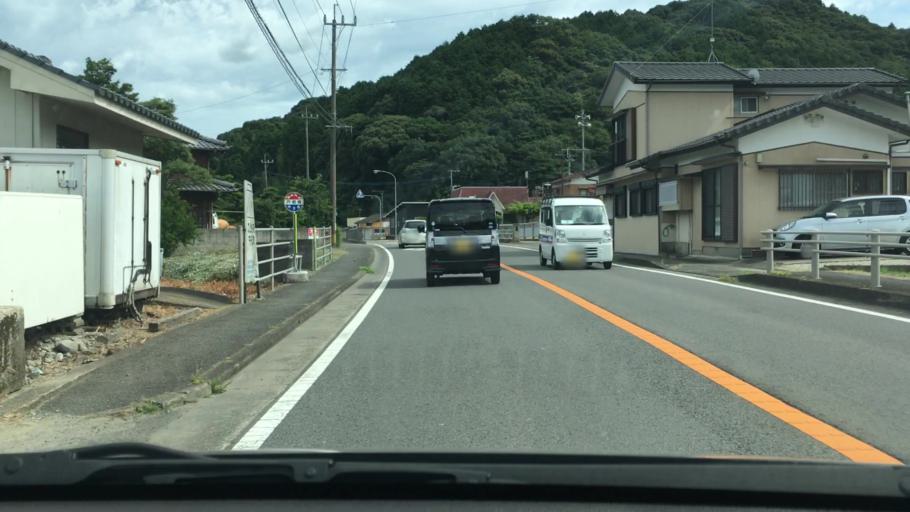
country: JP
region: Nagasaki
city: Togitsu
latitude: 32.8933
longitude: 129.7806
